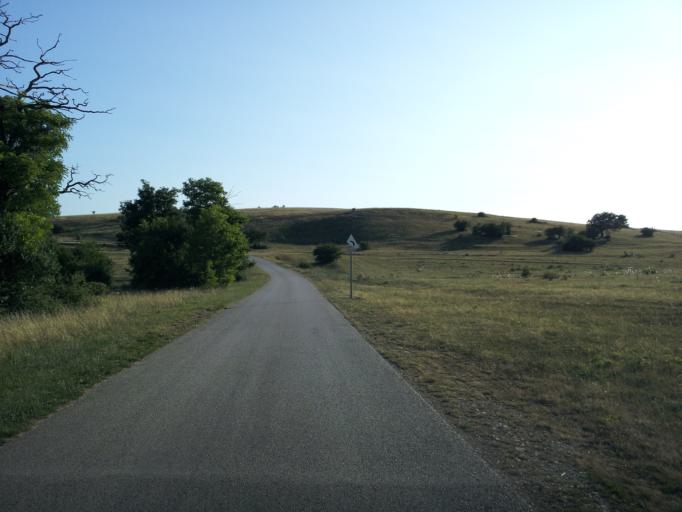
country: HU
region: Veszprem
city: Urkut
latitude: 46.9961
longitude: 17.6088
